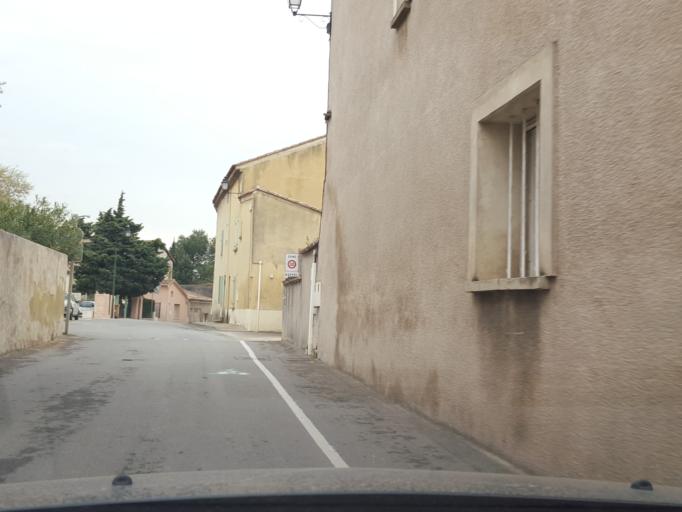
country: FR
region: Provence-Alpes-Cote d'Azur
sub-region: Departement du Vaucluse
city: Saint-Saturnin-les-Avignon
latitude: 43.9591
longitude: 4.9291
